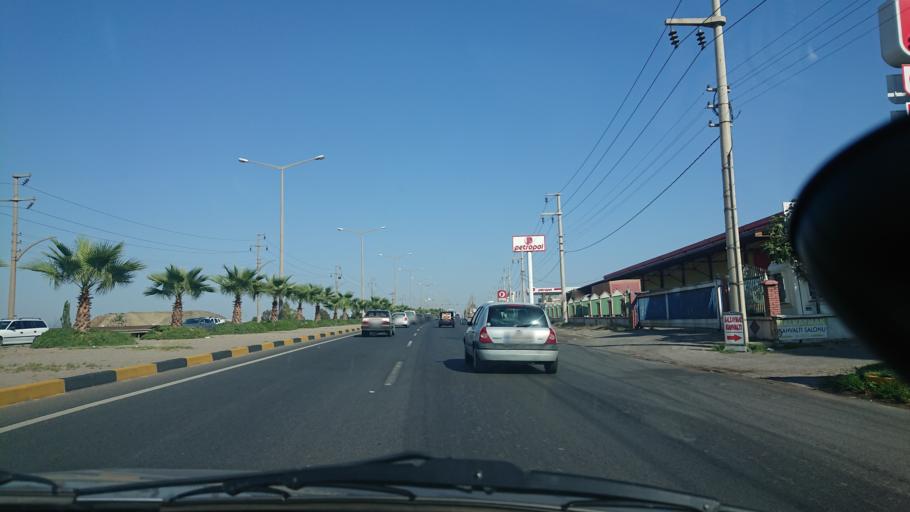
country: TR
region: Manisa
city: Turgutlu
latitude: 38.4957
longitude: 27.7358
